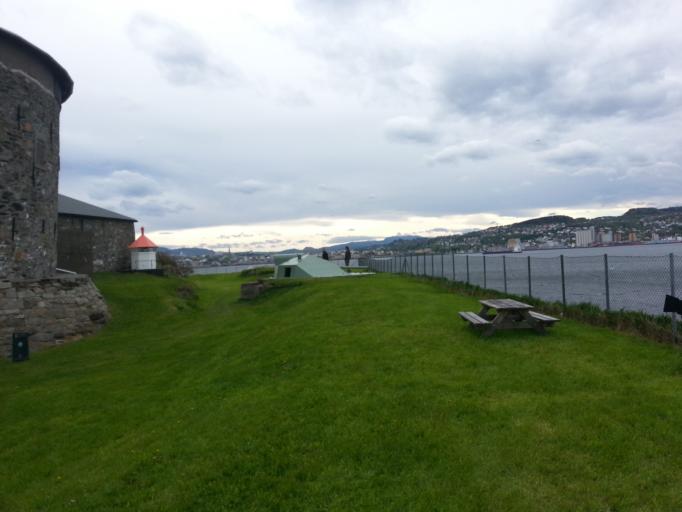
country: NO
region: Sor-Trondelag
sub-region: Trondheim
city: Trondheim
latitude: 63.4513
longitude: 10.3822
